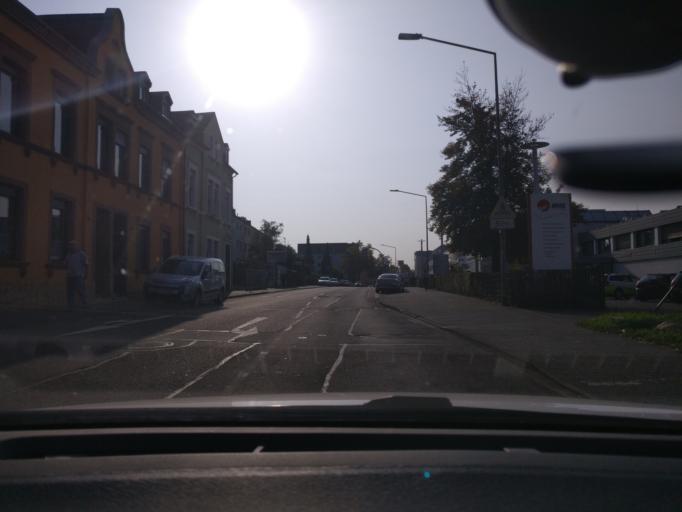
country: DE
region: Rheinland-Pfalz
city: Trier
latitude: 49.7590
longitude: 6.6580
